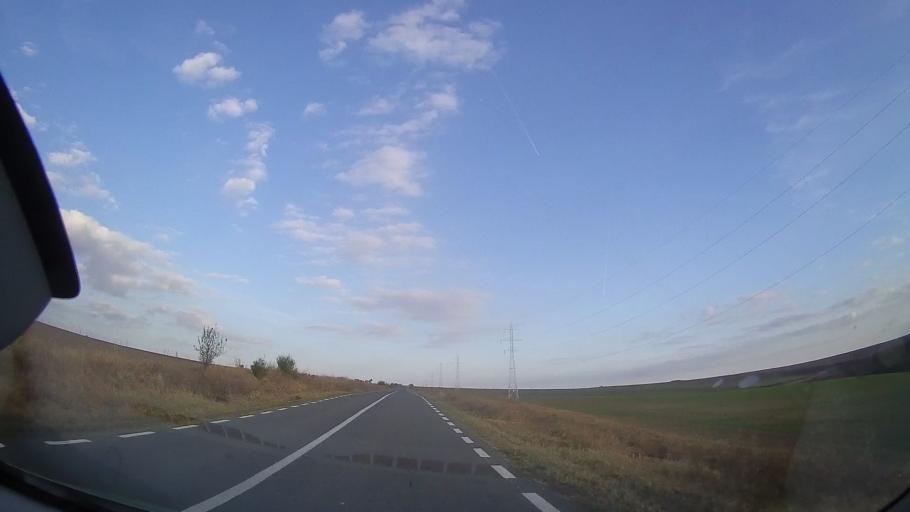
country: RO
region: Constanta
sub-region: Comuna Chirnogeni
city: Plopeni
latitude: 43.9524
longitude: 28.1583
